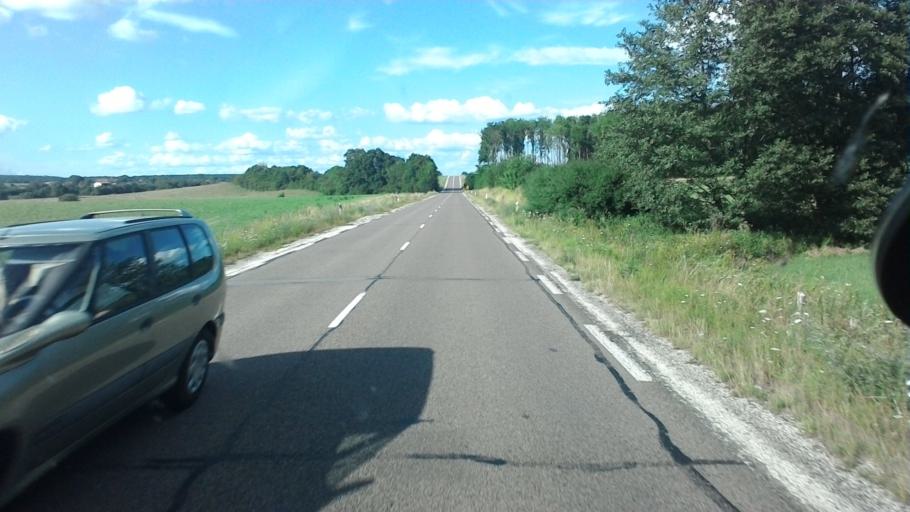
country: FR
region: Franche-Comte
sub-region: Departement de la Haute-Saone
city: Luxeuil-les-Bains
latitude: 47.7116
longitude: 6.2974
